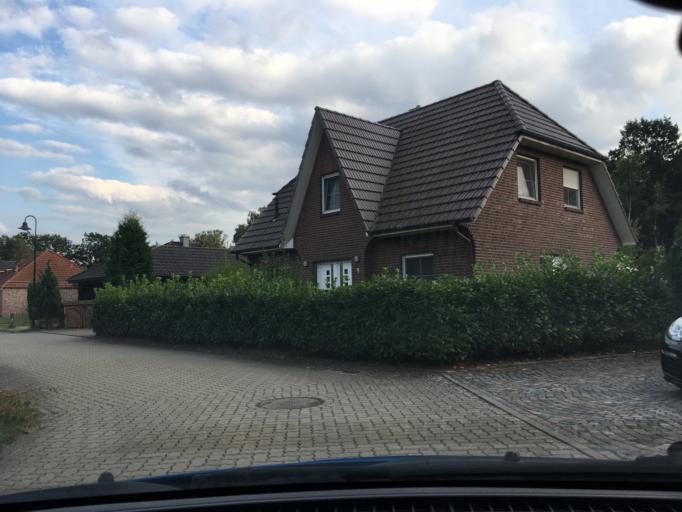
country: DE
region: Lower Saxony
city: Vierhofen
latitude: 53.2726
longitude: 10.2116
